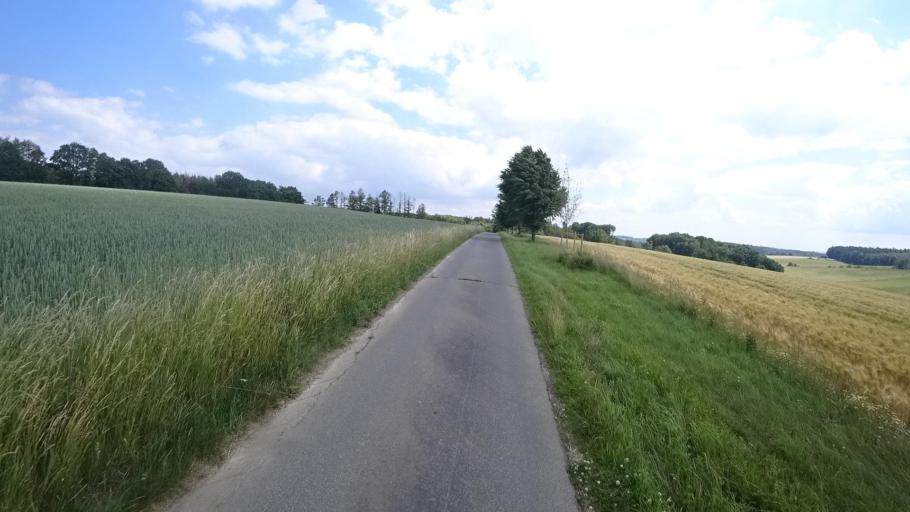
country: DE
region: Rheinland-Pfalz
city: Heupelzen
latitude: 50.7098
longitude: 7.6091
